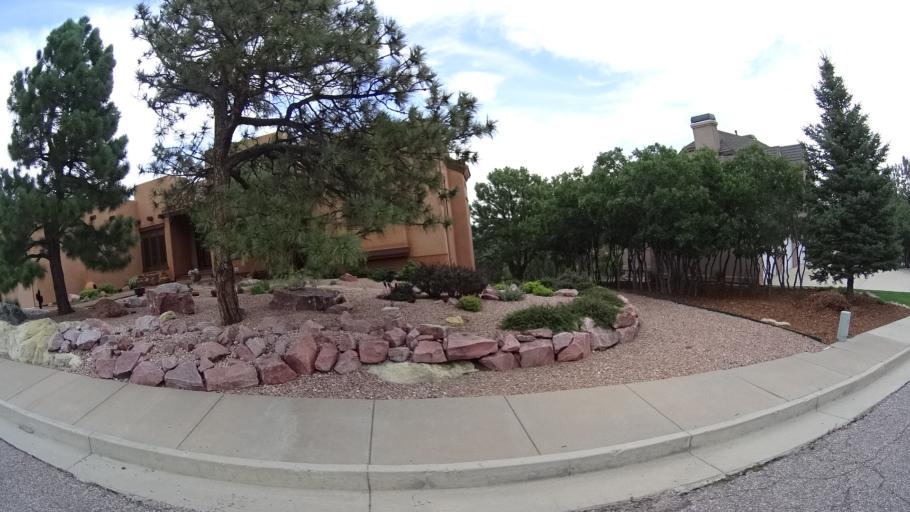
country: US
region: Colorado
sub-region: El Paso County
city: Colorado Springs
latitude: 38.9085
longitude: -104.8516
